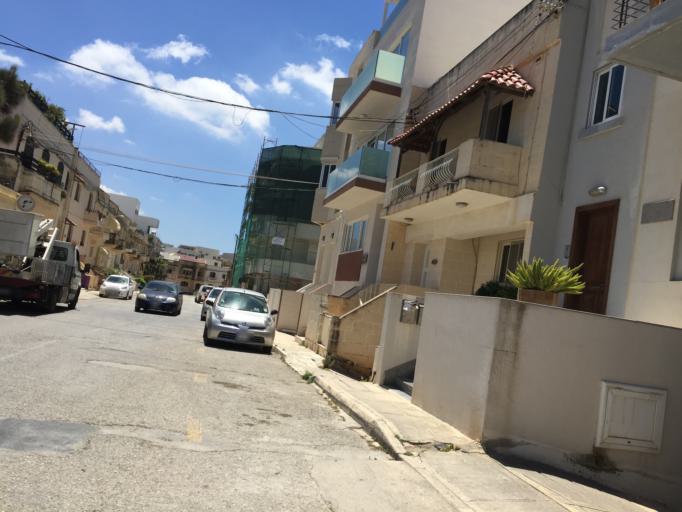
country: MT
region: Is-Swieqi
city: Swieqi
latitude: 35.9217
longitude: 14.4823
